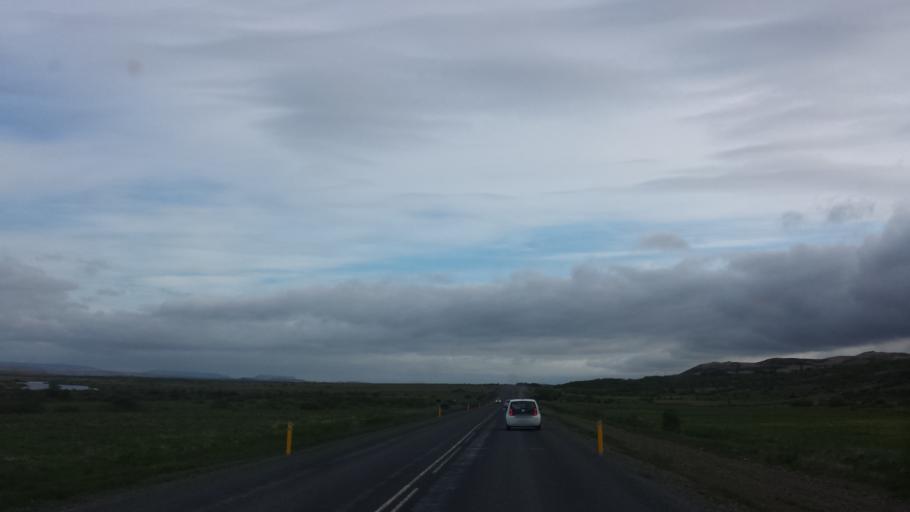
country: IS
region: South
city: Selfoss
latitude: 64.2962
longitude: -20.3340
